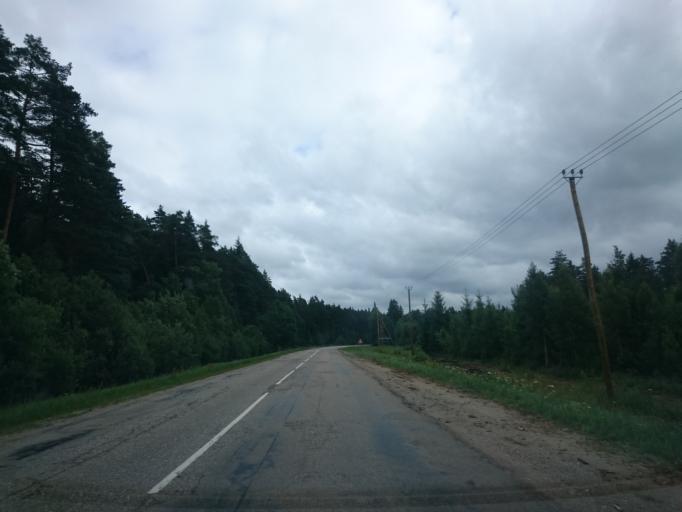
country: LV
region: Pavilostas
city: Pavilosta
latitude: 56.7925
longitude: 21.2421
